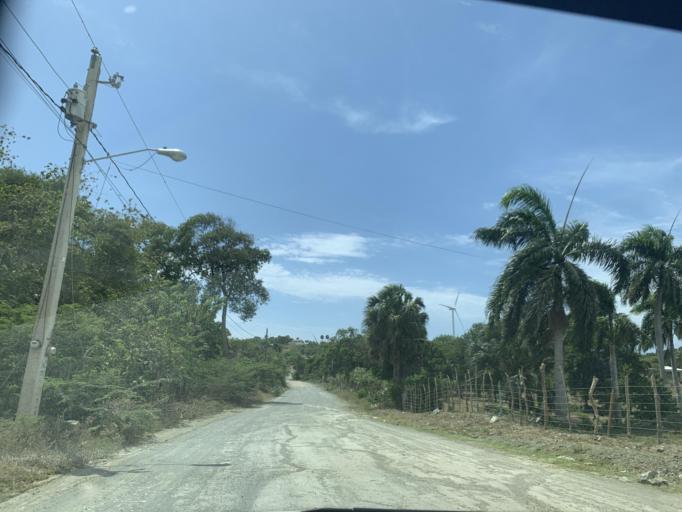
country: DO
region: Puerto Plata
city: Imbert
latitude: 19.8634
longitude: -70.8100
